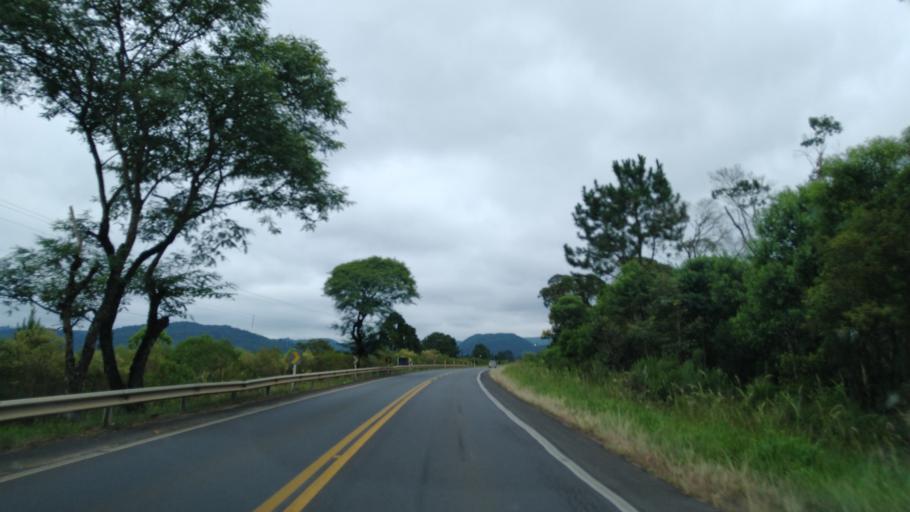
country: BR
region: Santa Catarina
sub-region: Porto Uniao
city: Porto Uniao
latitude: -26.2855
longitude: -51.0202
